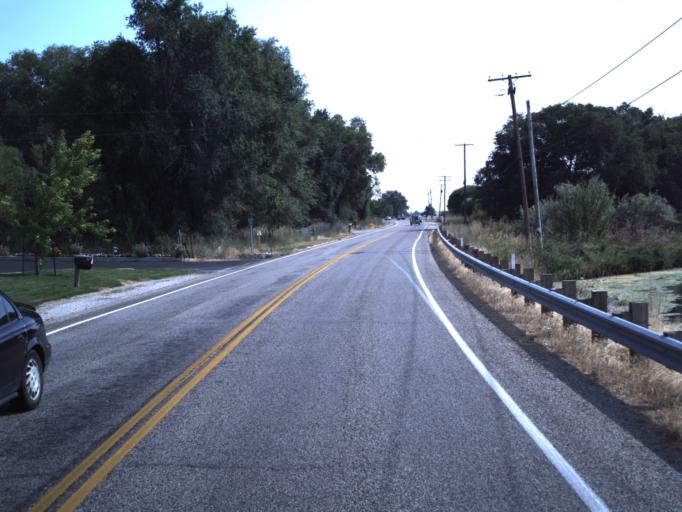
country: US
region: Utah
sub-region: Box Elder County
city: Honeyville
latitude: 41.5957
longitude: -112.0456
